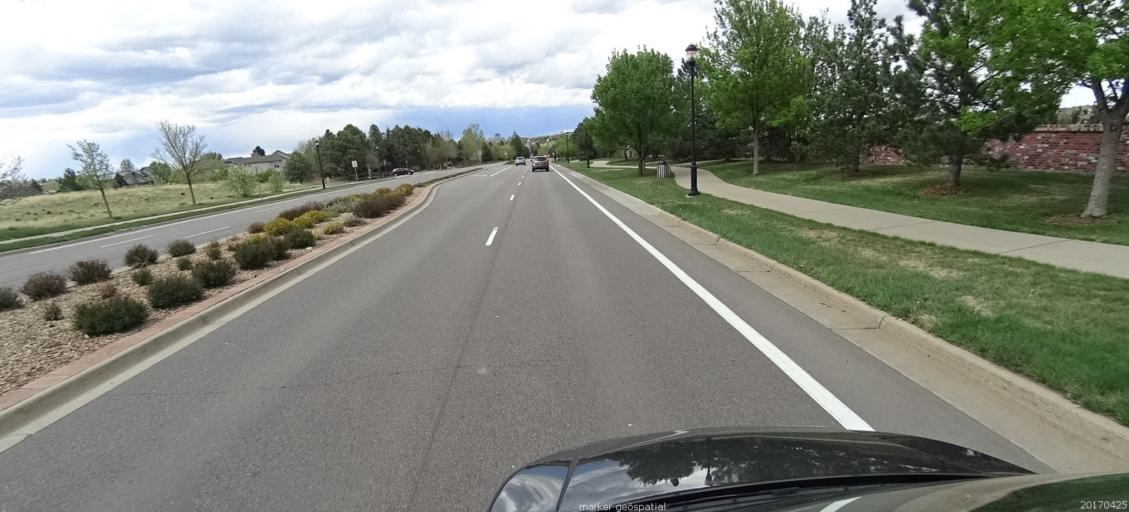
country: US
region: Colorado
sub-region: Adams County
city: Lone Tree
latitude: 39.5406
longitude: -104.8855
